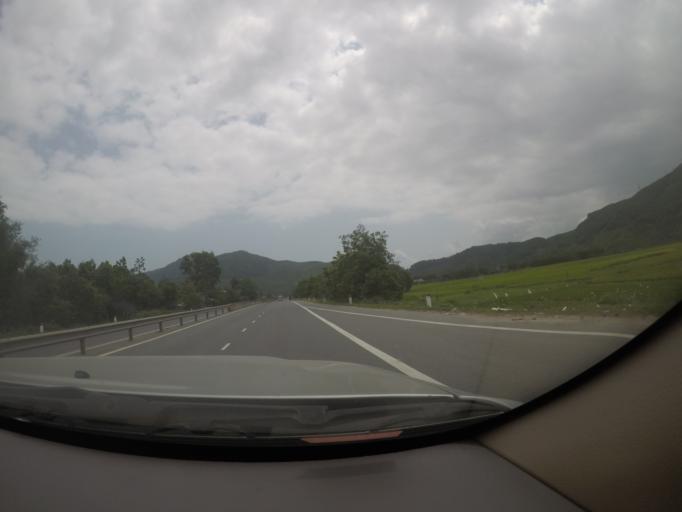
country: VN
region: Thua Thien-Hue
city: Phu Loc
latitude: 16.2701
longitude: 108.0219
